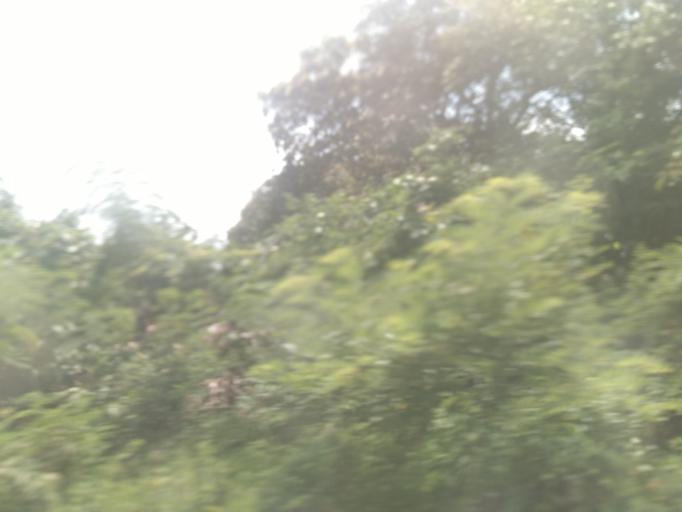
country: TZ
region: Zanzibar Urban/West
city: Zanzibar
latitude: -6.2854
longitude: 39.2834
